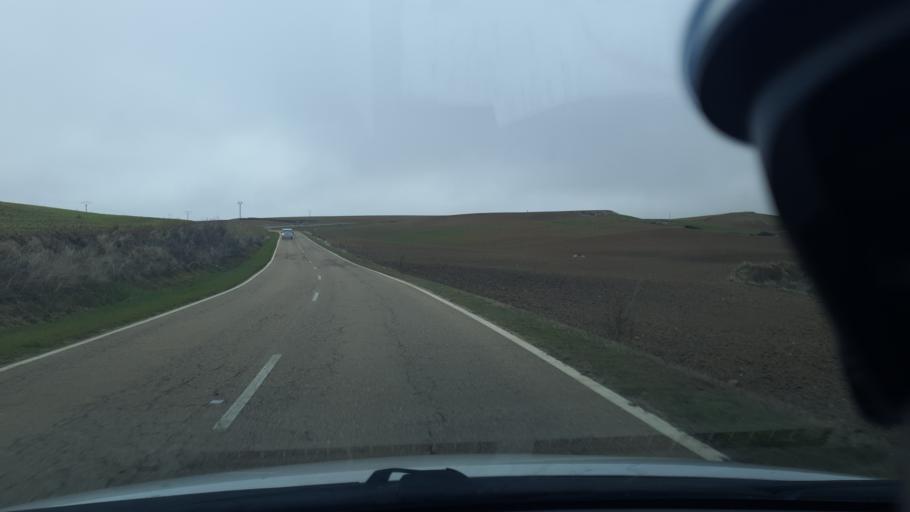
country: ES
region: Castille and Leon
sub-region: Provincia de Segovia
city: Hontanares de Eresma
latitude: 40.9890
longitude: -4.1998
